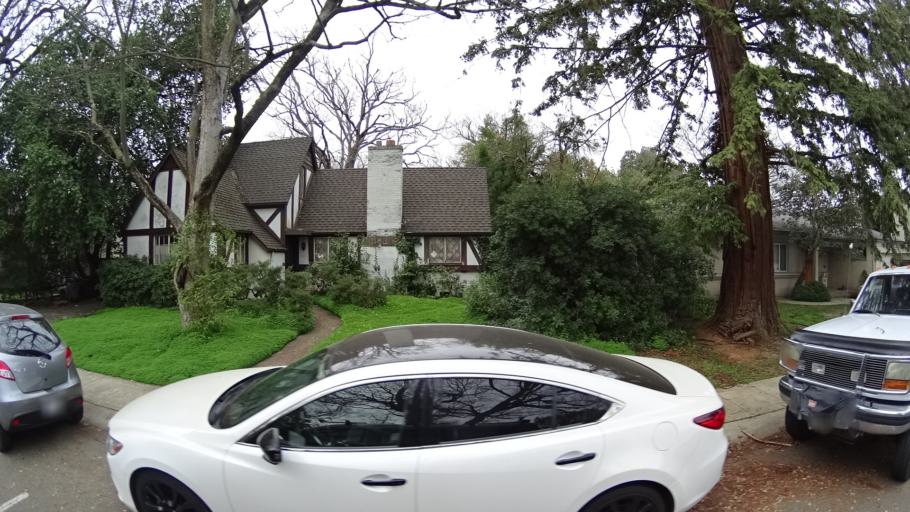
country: US
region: California
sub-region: Yolo County
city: Davis
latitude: 38.5418
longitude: -121.7452
